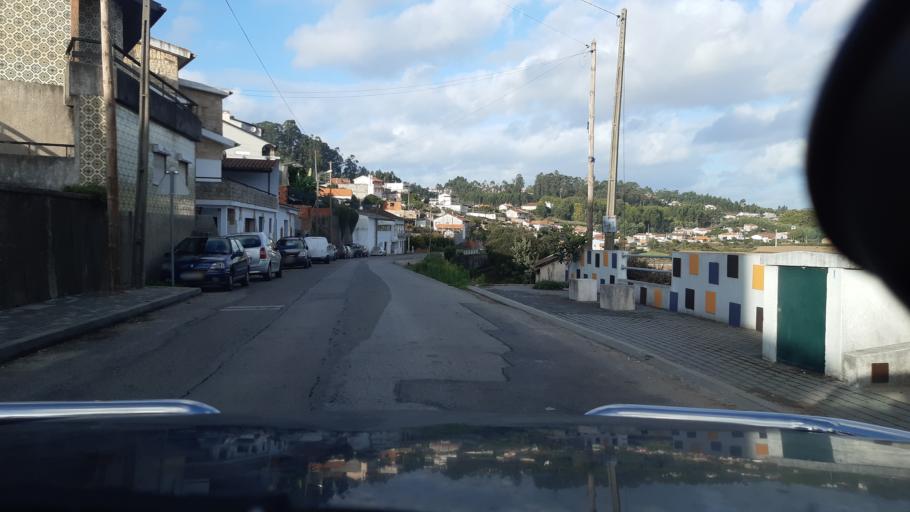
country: PT
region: Aveiro
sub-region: Agueda
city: Agueda
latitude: 40.5723
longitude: -8.4713
